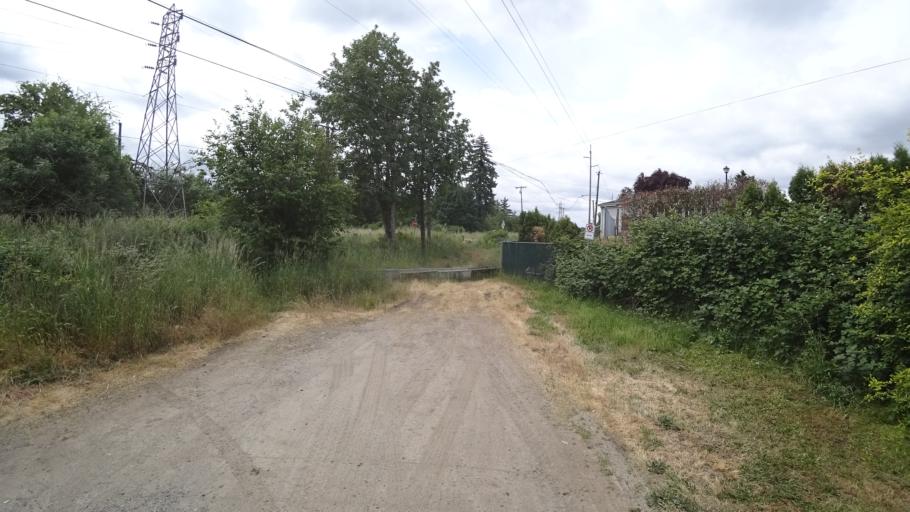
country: US
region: Oregon
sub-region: Multnomah County
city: Lents
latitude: 45.4672
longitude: -122.5751
